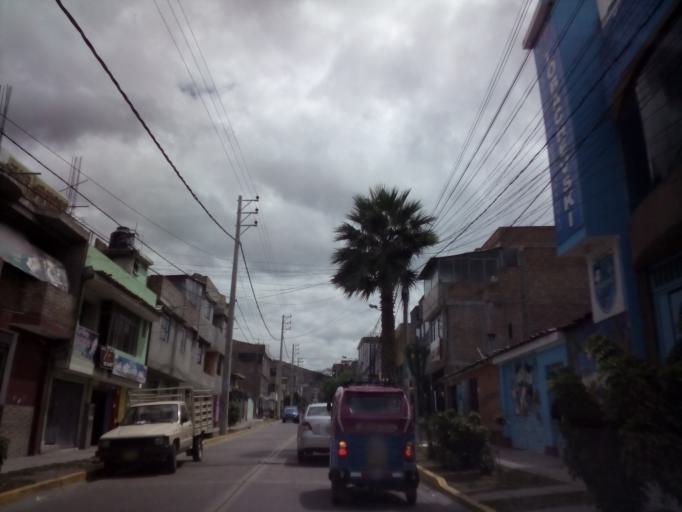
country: PE
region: Ayacucho
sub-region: Provincia de Huamanga
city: Ayacucho
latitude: -13.1506
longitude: -74.2286
